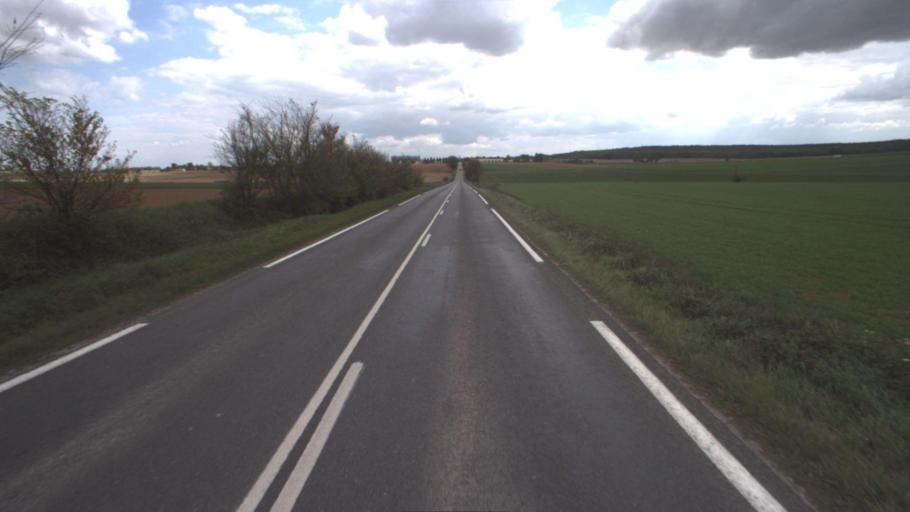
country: FR
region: Ile-de-France
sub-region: Departement de Seine-et-Marne
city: Saint-Soupplets
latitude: 49.0503
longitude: 2.7885
